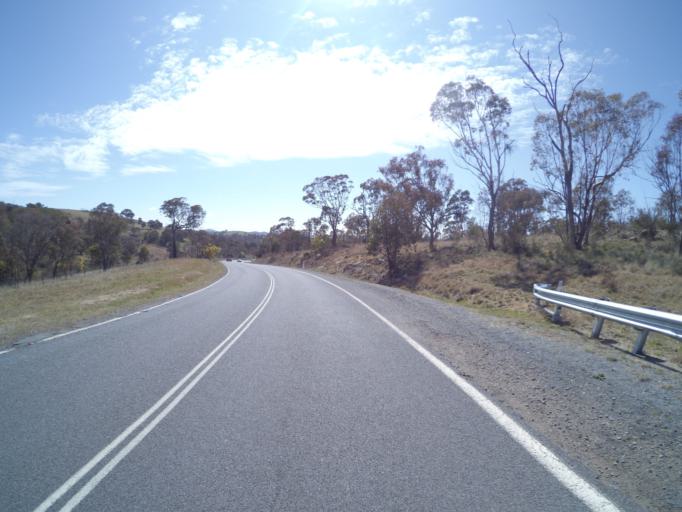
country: AU
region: Australian Capital Territory
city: Macarthur
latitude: -35.4599
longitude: 149.0365
